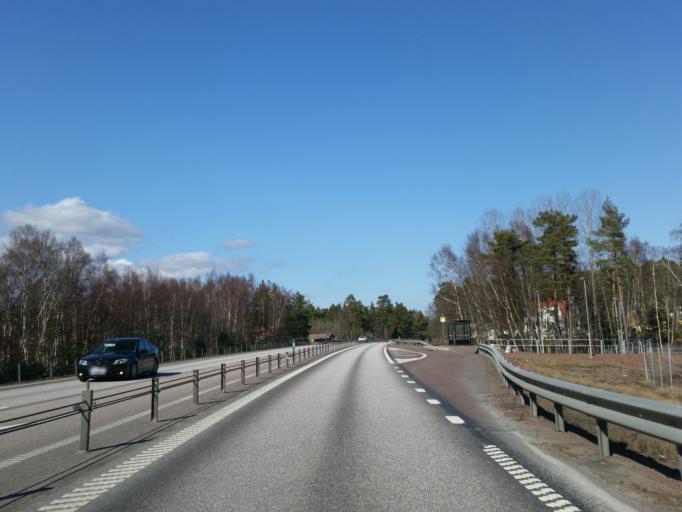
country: SE
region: Kalmar
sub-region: Oskarshamns Kommun
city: Paskallavik
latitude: 57.1645
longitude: 16.4445
